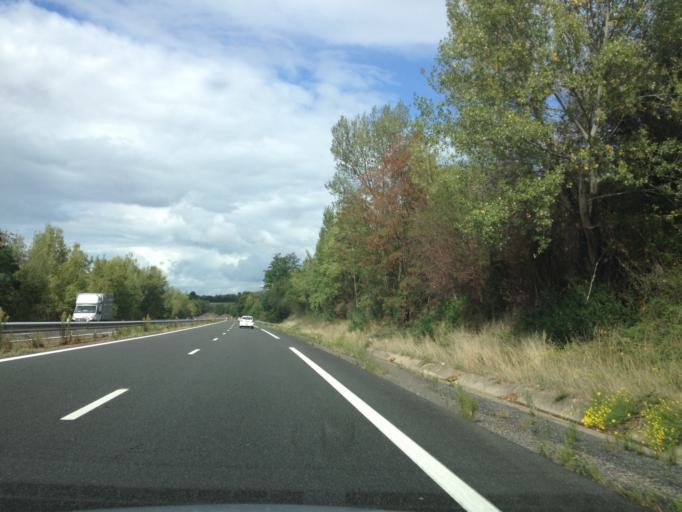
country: FR
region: Rhone-Alpes
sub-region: Departement de la Loire
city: Le Coteau
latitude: 45.9894
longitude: 4.1169
